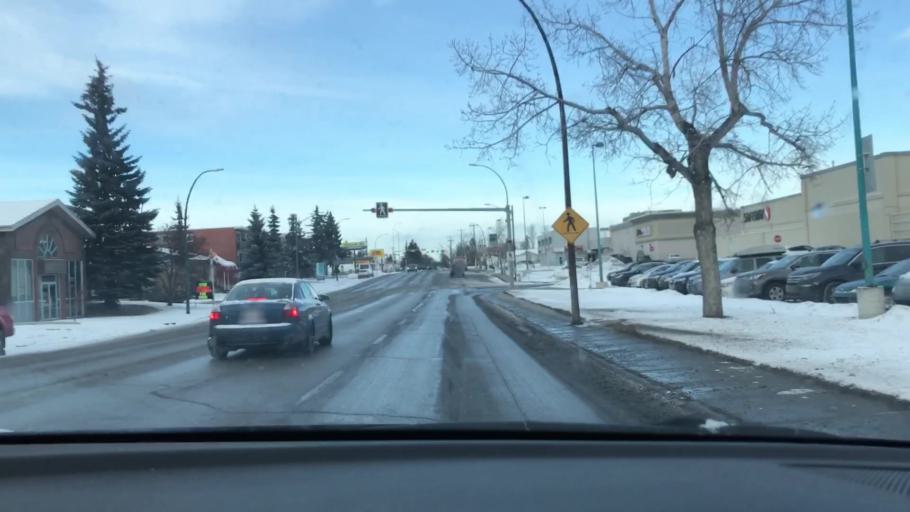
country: CA
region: Alberta
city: Calgary
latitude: 51.0426
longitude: -114.1411
